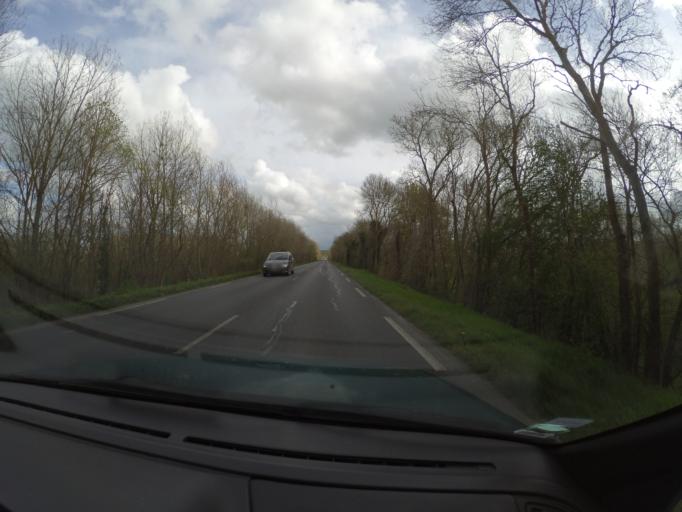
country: FR
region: Pays de la Loire
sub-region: Departement de Maine-et-Loire
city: Lire
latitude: 47.3531
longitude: -1.1701
